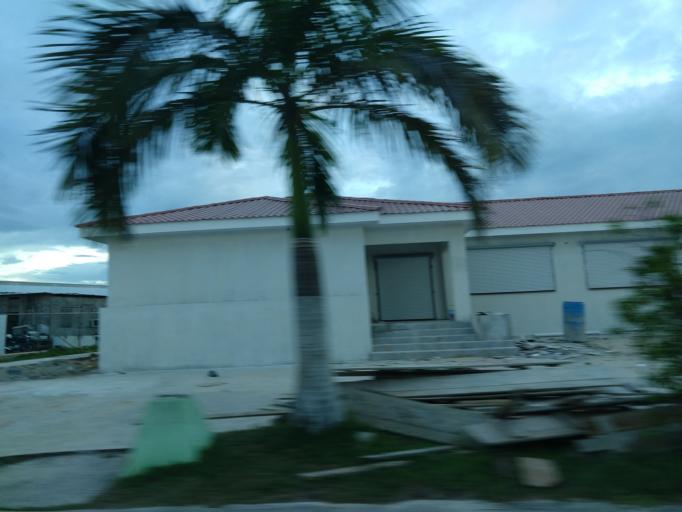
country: BZ
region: Belize
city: Belize City
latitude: 17.5038
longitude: -88.1881
